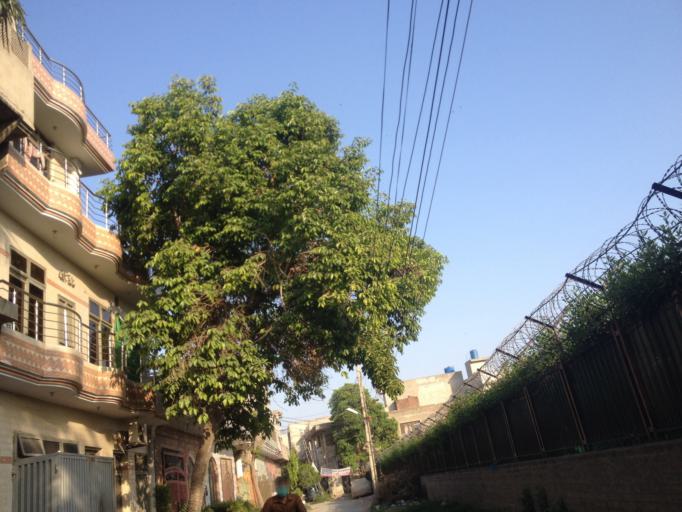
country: PK
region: Punjab
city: Lahore
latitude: 31.5552
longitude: 74.4013
